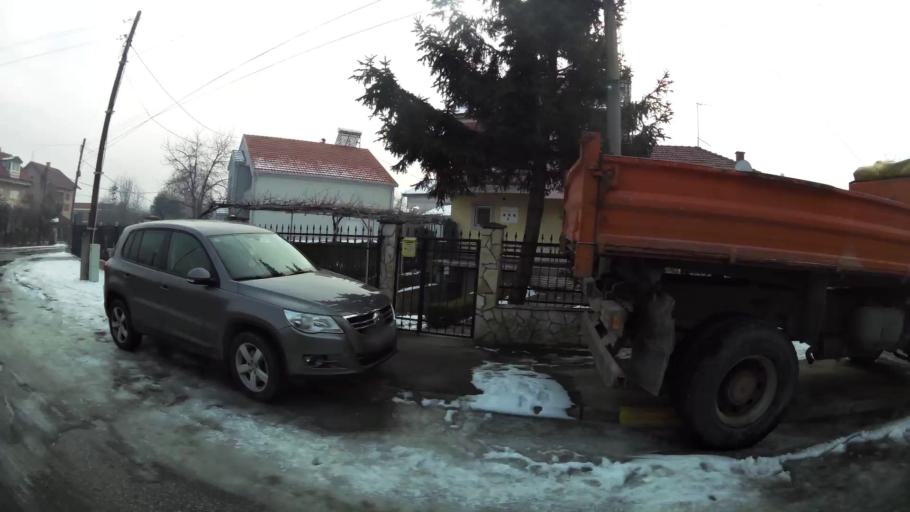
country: MK
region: Kisela Voda
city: Kisela Voda
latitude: 41.9970
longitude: 21.5056
